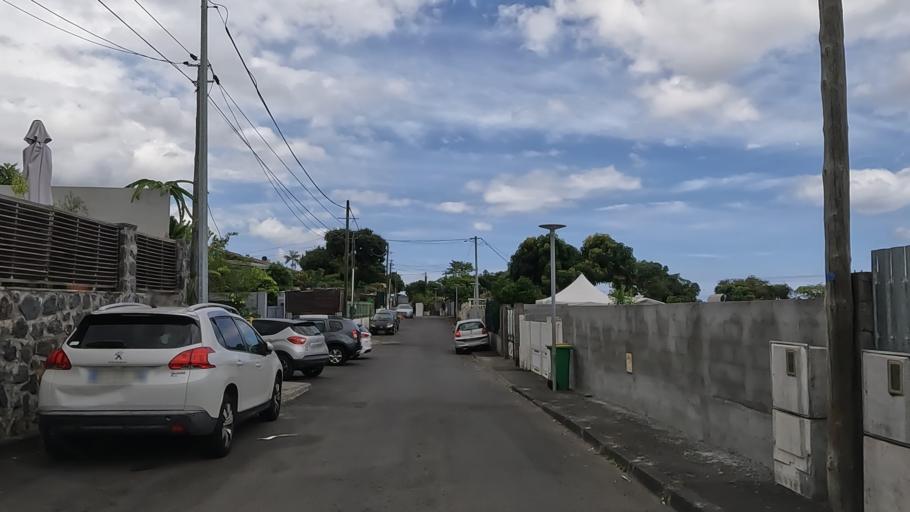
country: RE
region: Reunion
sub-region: Reunion
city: La Possession
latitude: -20.9597
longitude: 55.3362
